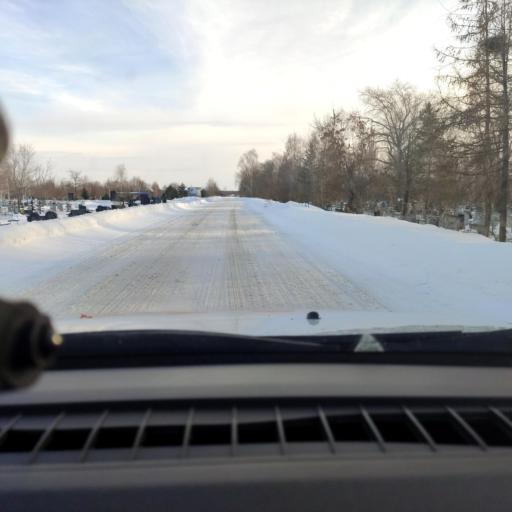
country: RU
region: Samara
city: Chapayevsk
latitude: 52.9899
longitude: 49.7448
